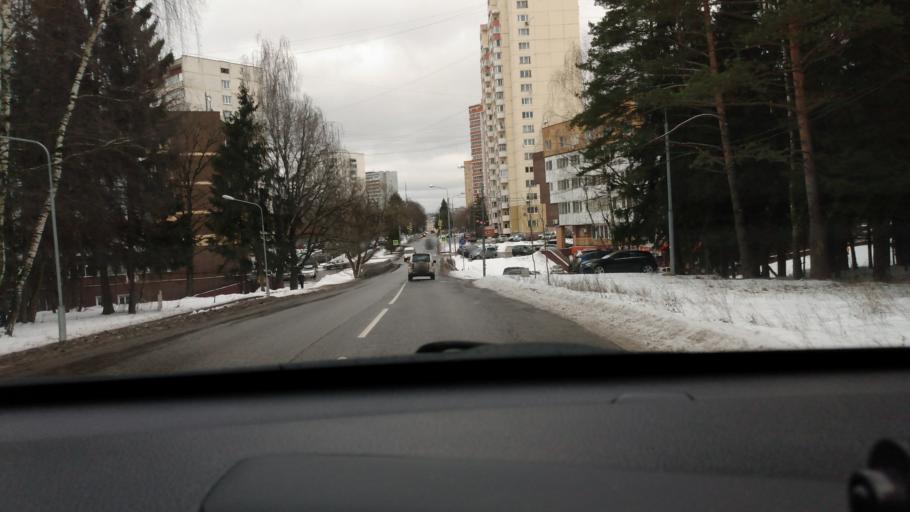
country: RU
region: Moskovskaya
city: Troitsk
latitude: 55.4860
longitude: 37.2950
